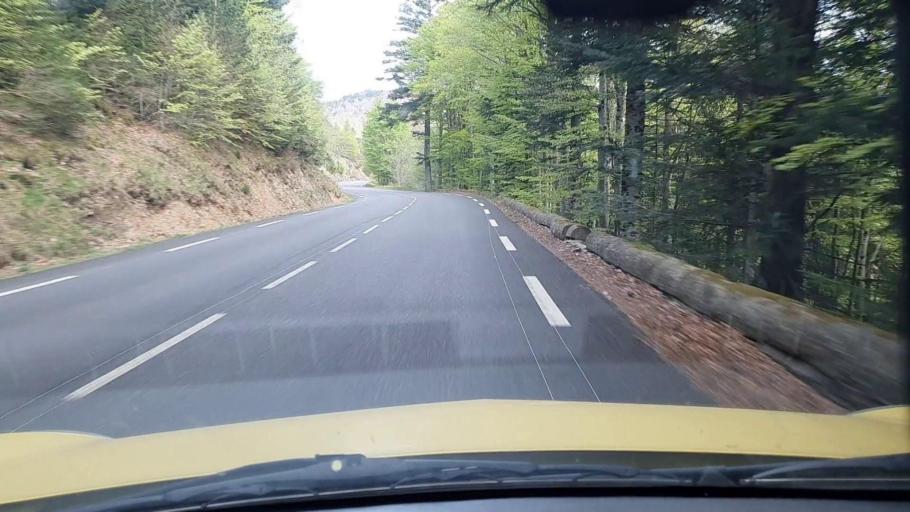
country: FR
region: Languedoc-Roussillon
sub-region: Departement du Gard
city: Valleraugue
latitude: 44.0955
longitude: 3.5552
